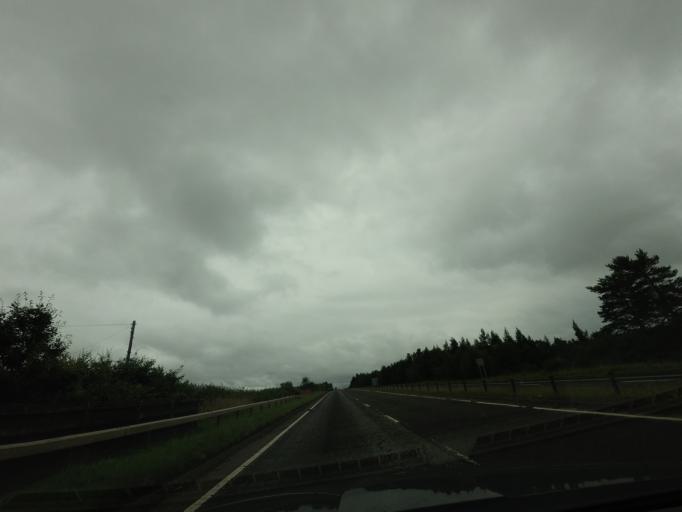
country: GB
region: Scotland
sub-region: Highland
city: Inverness
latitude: 57.4479
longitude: -4.1538
